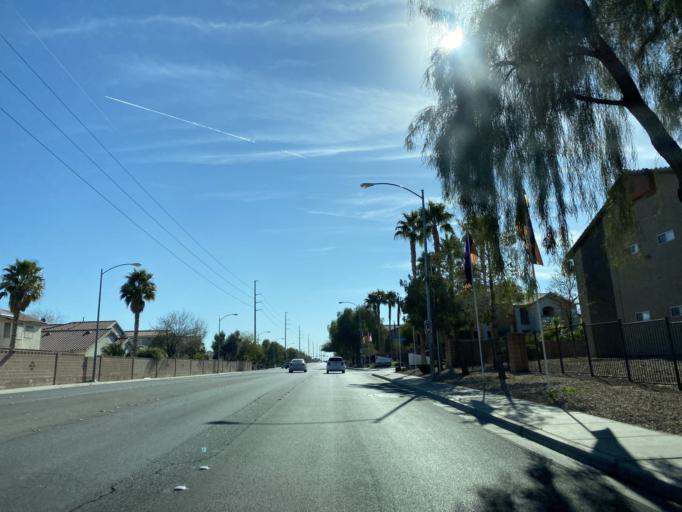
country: US
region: Nevada
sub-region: Clark County
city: North Las Vegas
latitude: 36.2372
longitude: -115.1437
